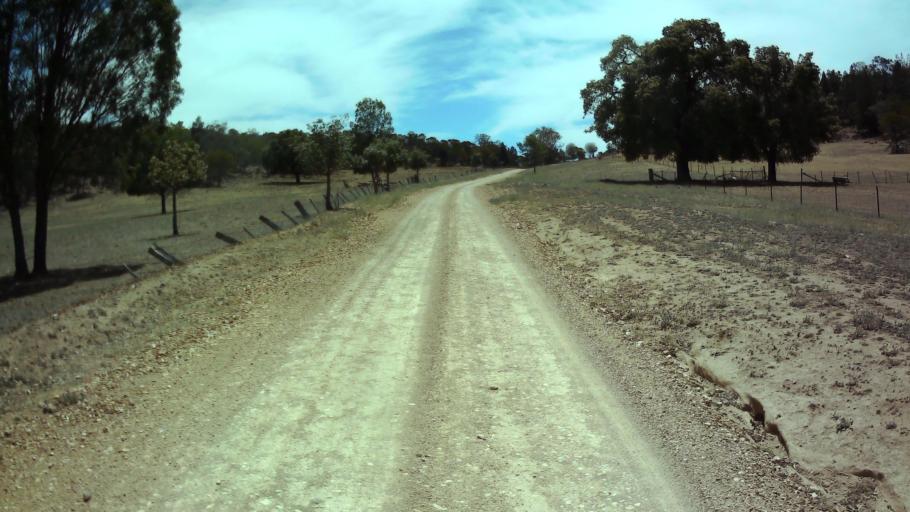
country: AU
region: New South Wales
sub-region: Weddin
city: Grenfell
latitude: -33.7472
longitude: 148.1839
